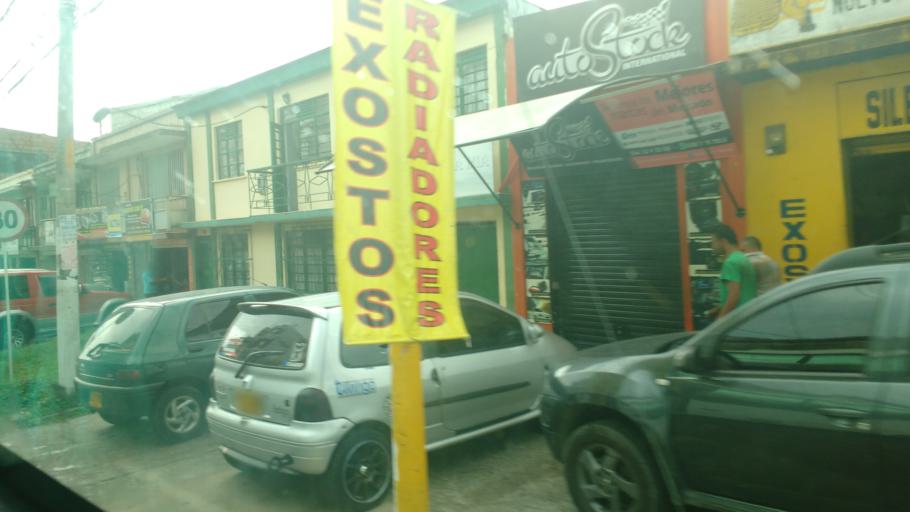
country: CO
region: Risaralda
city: Pereira
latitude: 4.8125
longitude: -75.7056
